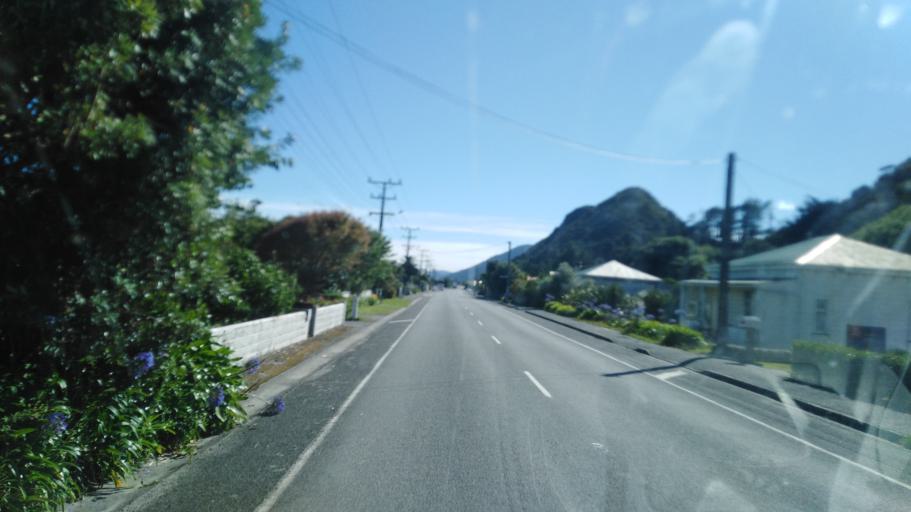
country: NZ
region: West Coast
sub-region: Buller District
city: Westport
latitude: -41.6318
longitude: 171.8521
